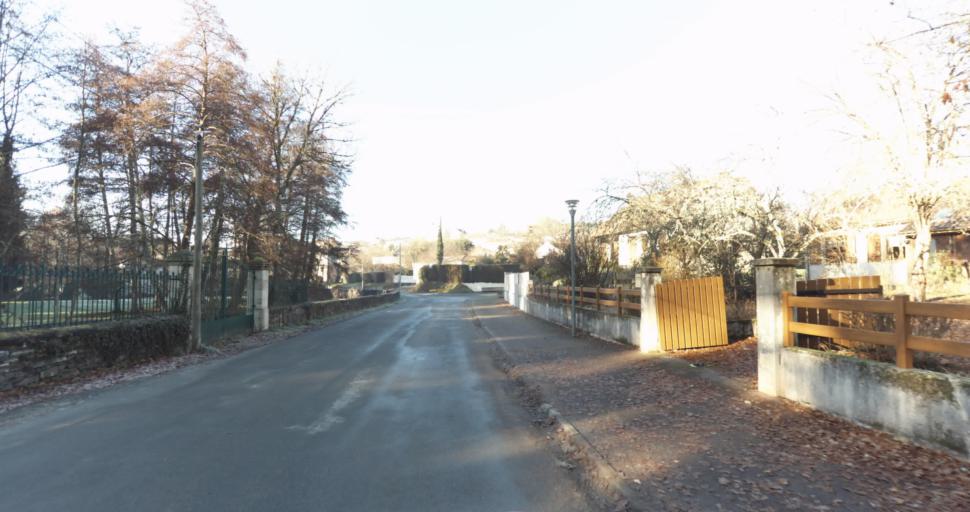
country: FR
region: Limousin
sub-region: Departement de la Haute-Vienne
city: Aixe-sur-Vienne
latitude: 45.7995
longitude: 1.1534
